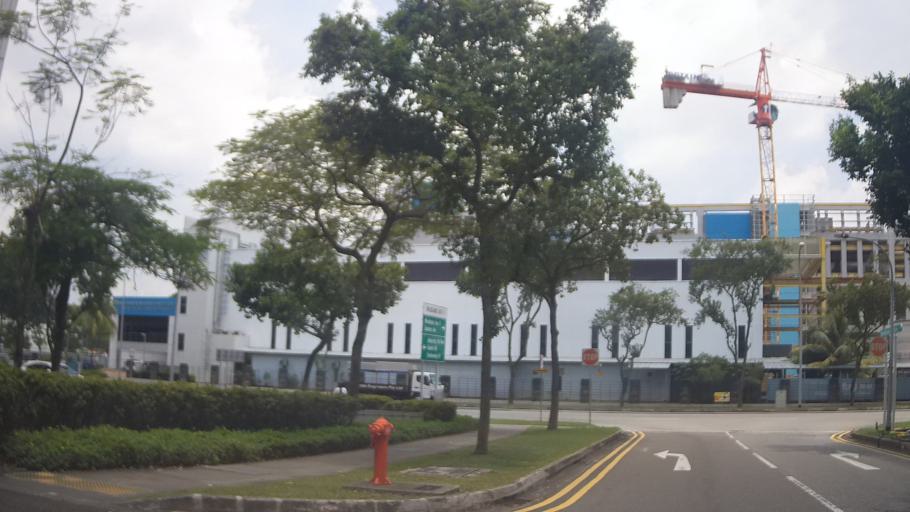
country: MY
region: Johor
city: Johor Bahru
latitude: 1.4554
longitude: 103.7996
